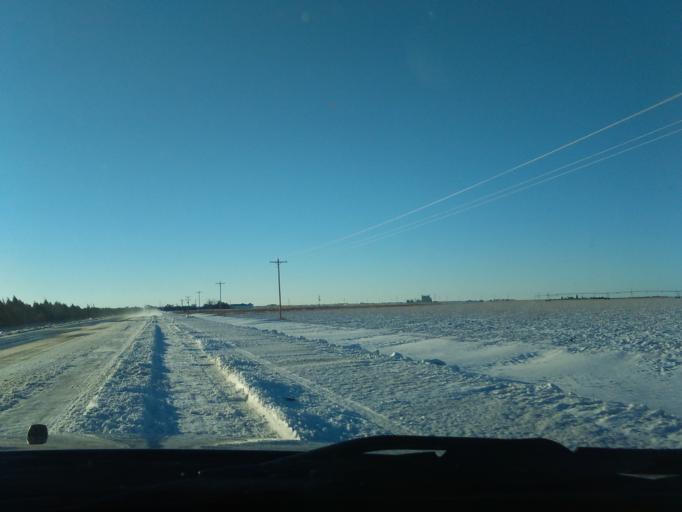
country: US
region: Colorado
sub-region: Phillips County
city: Holyoke
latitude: 40.5856
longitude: -102.2300
